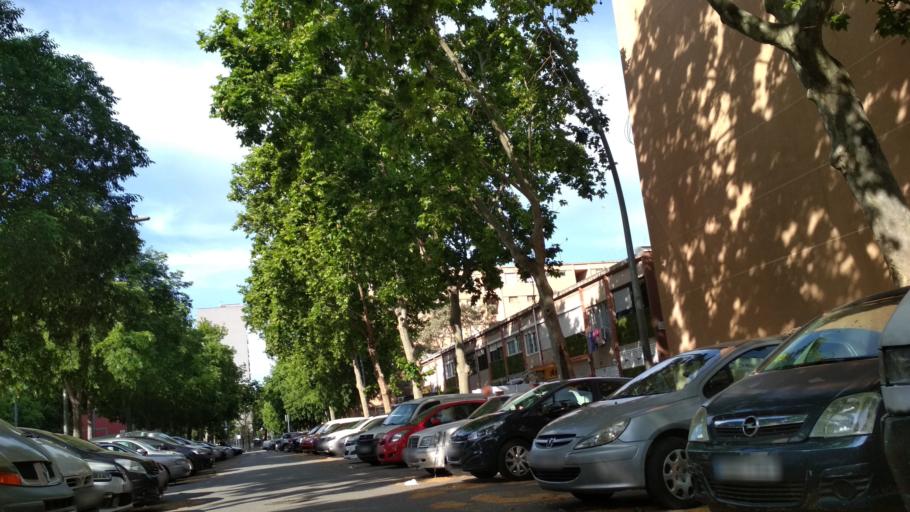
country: ES
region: Catalonia
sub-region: Provincia de Barcelona
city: Sant Adria de Besos
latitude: 41.4197
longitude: 2.2133
